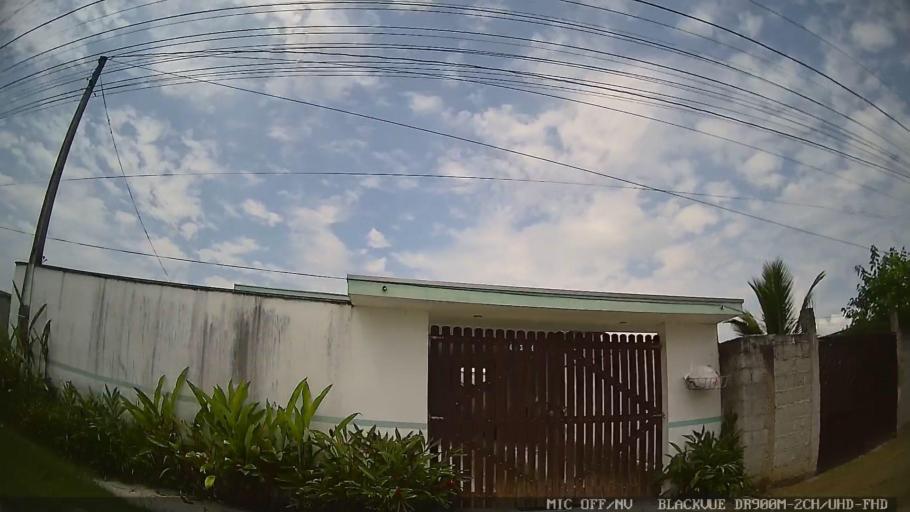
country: BR
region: Sao Paulo
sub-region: Caraguatatuba
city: Caraguatatuba
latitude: -23.6691
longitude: -45.4566
